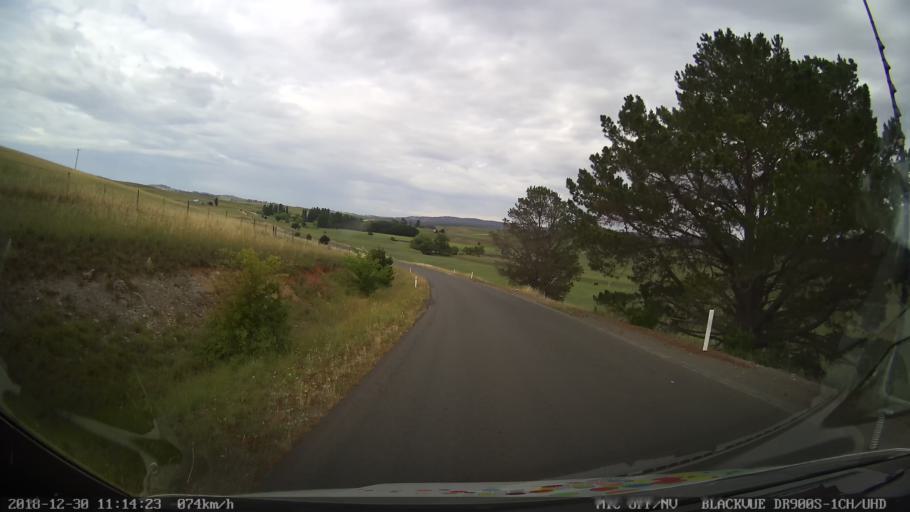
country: AU
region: New South Wales
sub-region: Snowy River
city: Jindabyne
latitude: -36.5349
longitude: 148.7300
